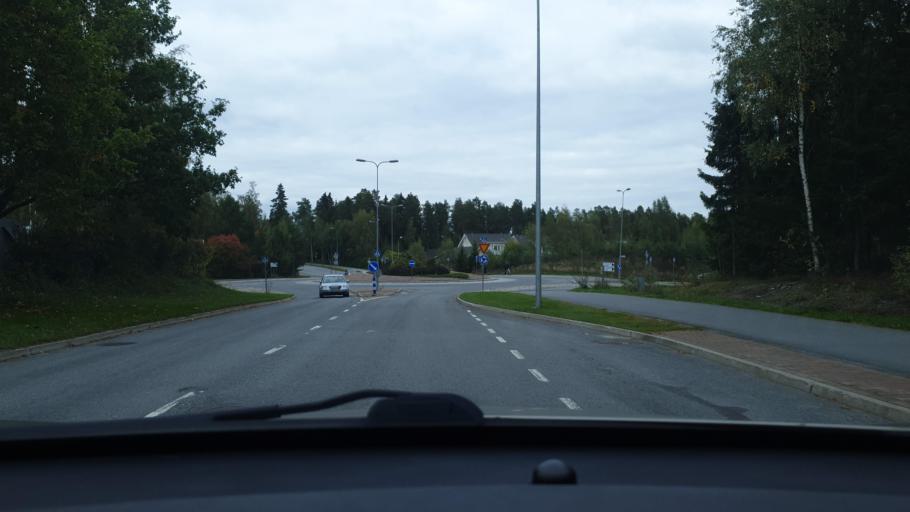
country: FI
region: Ostrobothnia
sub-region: Vaasa
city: Korsholm
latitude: 63.1027
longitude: 21.6770
